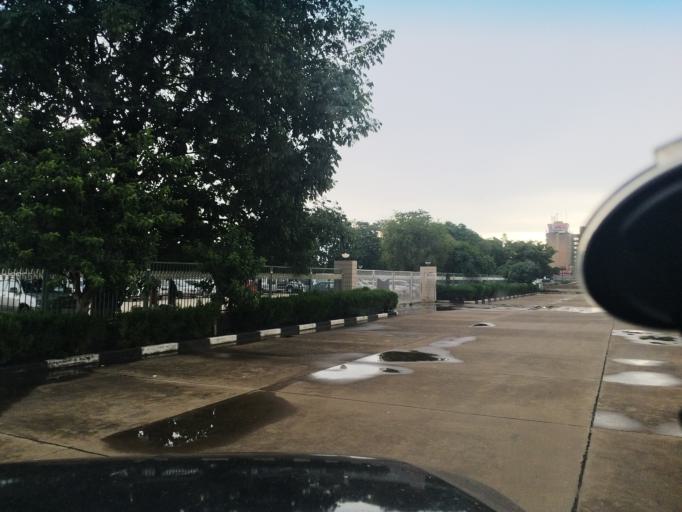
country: ZM
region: Lusaka
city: Lusaka
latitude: -15.4224
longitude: 28.2917
